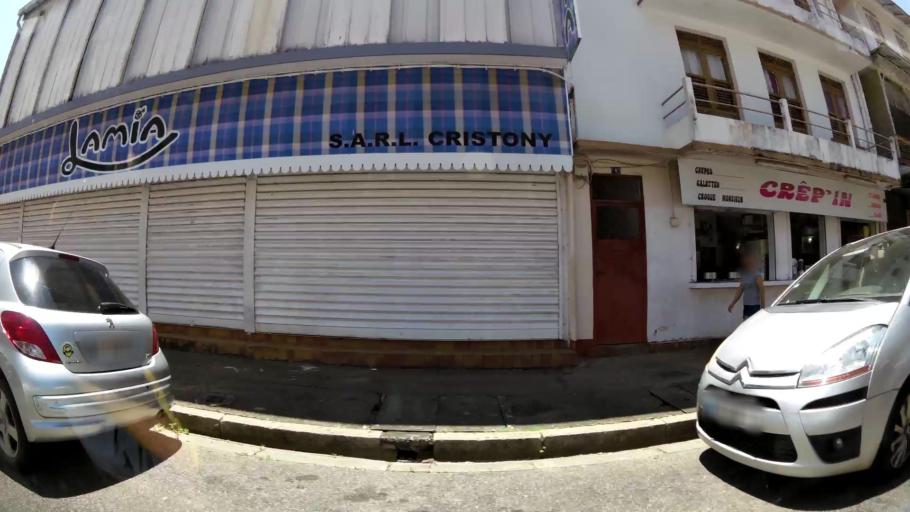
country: GF
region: Guyane
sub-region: Guyane
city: Cayenne
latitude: 4.9373
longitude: -52.3324
